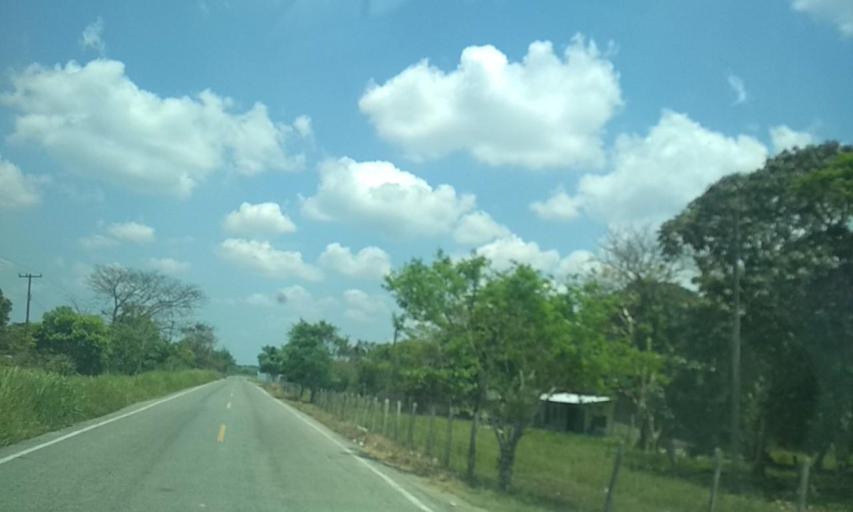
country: MX
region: Tabasco
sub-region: Huimanguillo
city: Huapacal 1ra. Seccion
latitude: 17.7538
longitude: -93.7238
